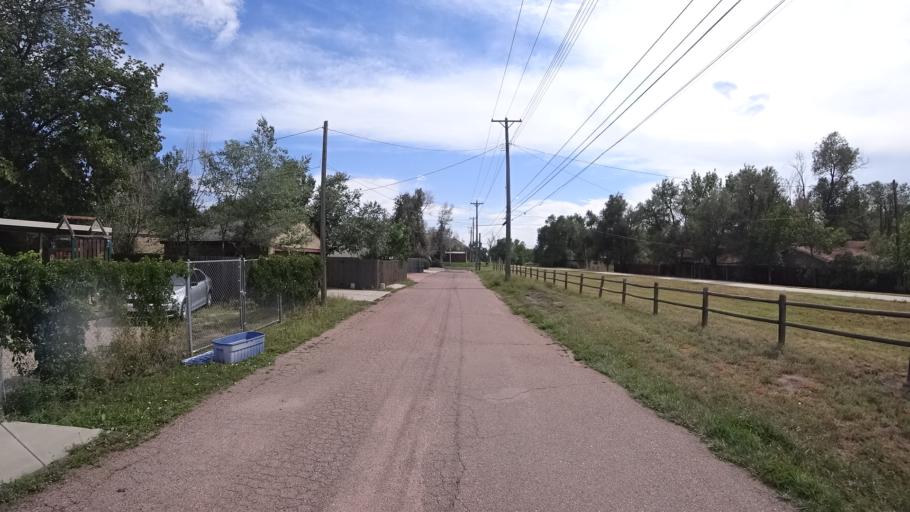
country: US
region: Colorado
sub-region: El Paso County
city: Colorado Springs
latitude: 38.8623
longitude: -104.8174
